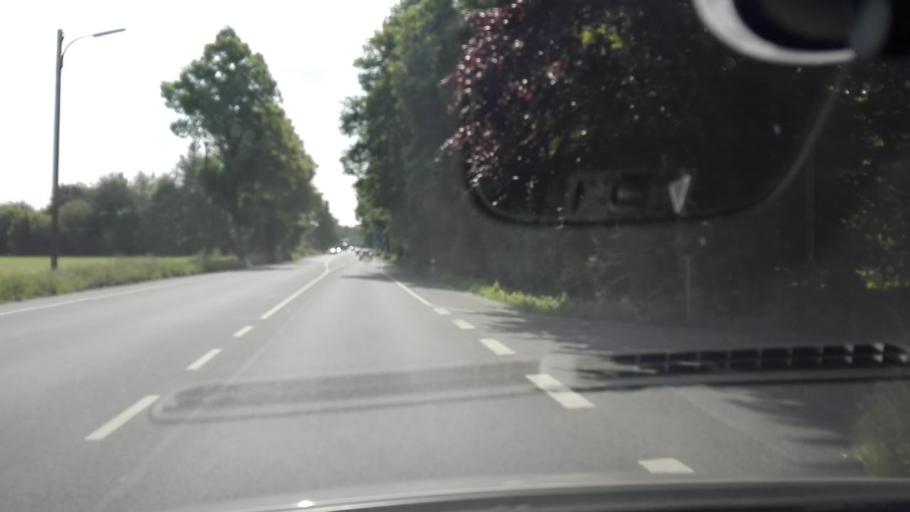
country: DE
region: North Rhine-Westphalia
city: Bergkamen
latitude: 51.5961
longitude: 7.6119
